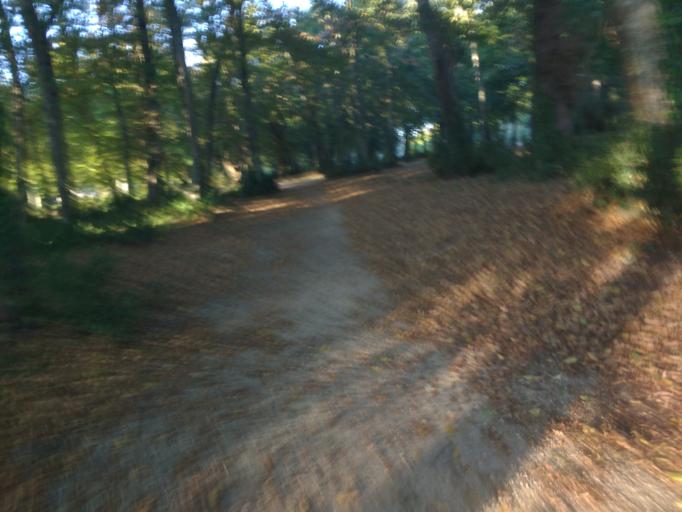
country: FR
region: Aquitaine
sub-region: Departement de la Gironde
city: Gradignan
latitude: 44.7772
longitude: -0.6023
